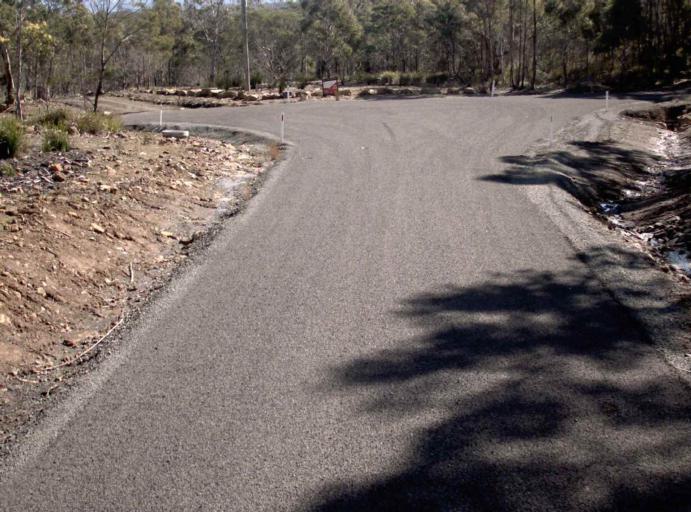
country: AU
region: Tasmania
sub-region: Launceston
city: Mayfield
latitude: -41.3168
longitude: 147.1149
